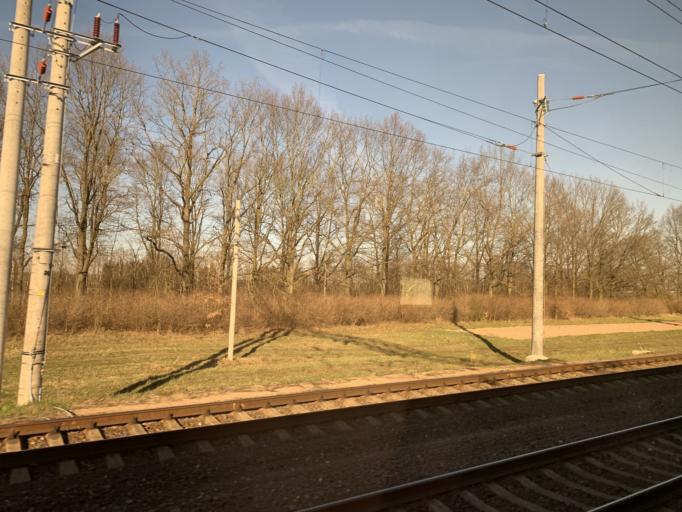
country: BY
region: Minsk
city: Turets-Bayary
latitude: 54.3682
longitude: 26.6572
